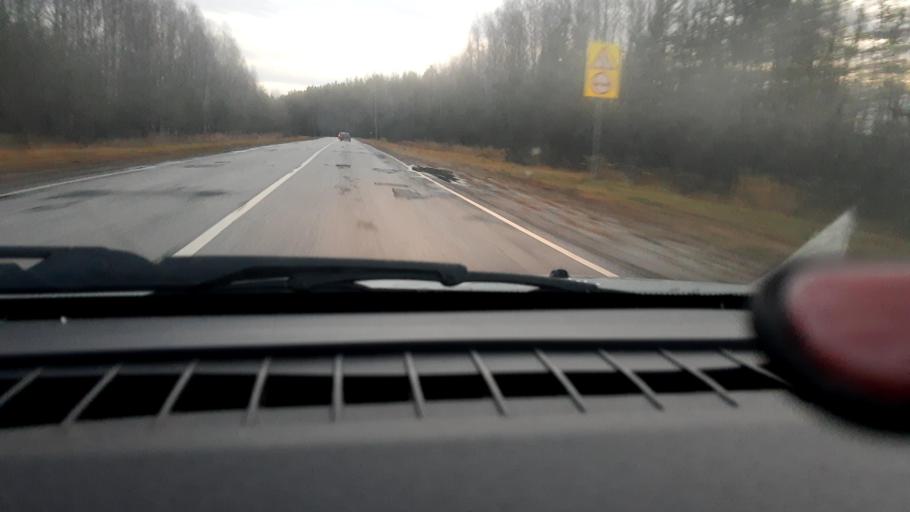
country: RU
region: Nizjnij Novgorod
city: Krasnyye Baki
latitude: 57.0075
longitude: 45.1120
